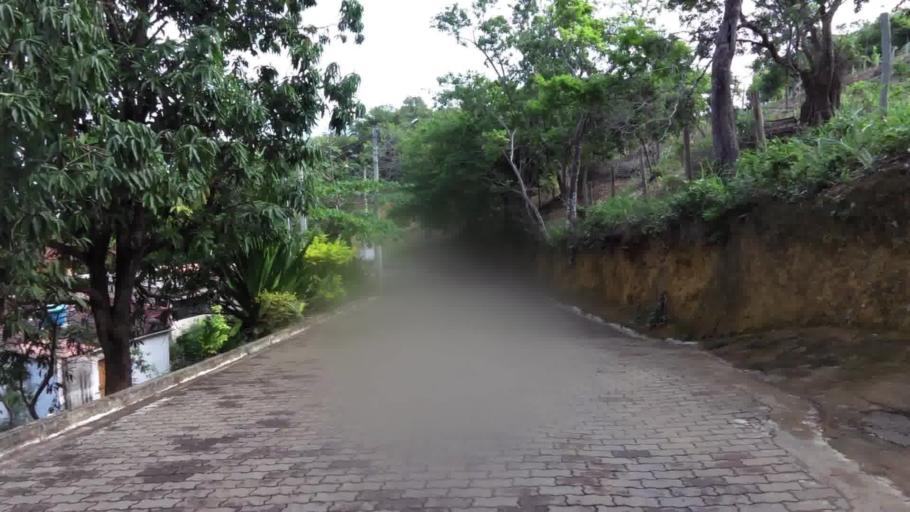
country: BR
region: Espirito Santo
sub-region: Piuma
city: Piuma
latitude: -20.8094
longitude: -40.6612
